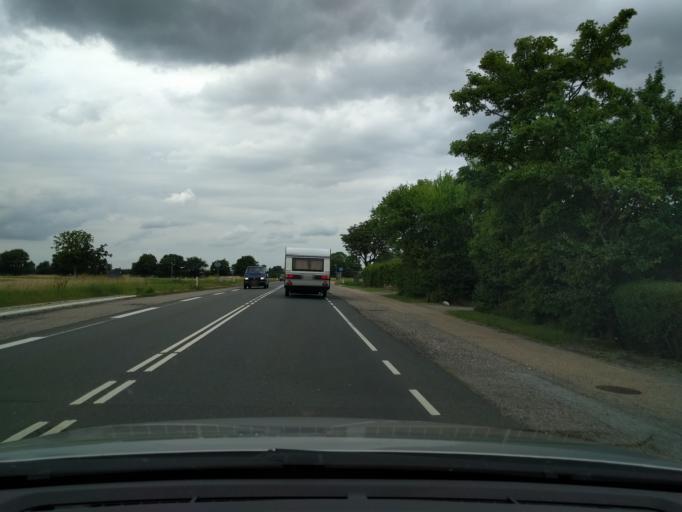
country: DK
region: Zealand
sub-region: Ringsted Kommune
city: Ringsted
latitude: 55.4228
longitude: 11.8237
